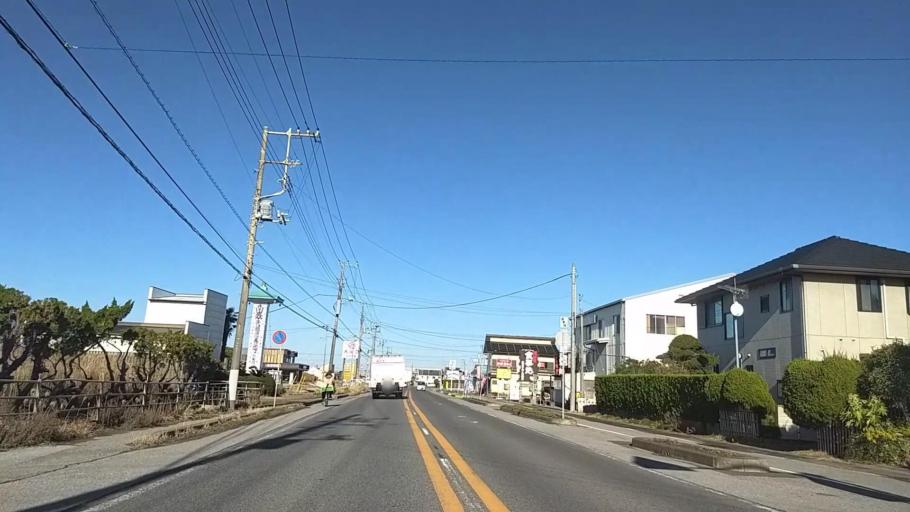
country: JP
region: Chiba
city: Togane
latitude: 35.5163
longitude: 140.4400
